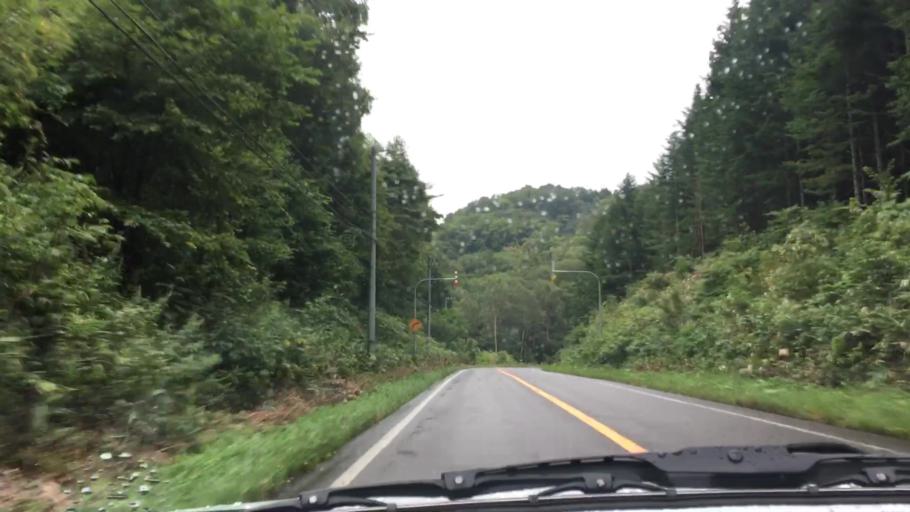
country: JP
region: Hokkaido
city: Niseko Town
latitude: 42.6158
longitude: 140.7288
